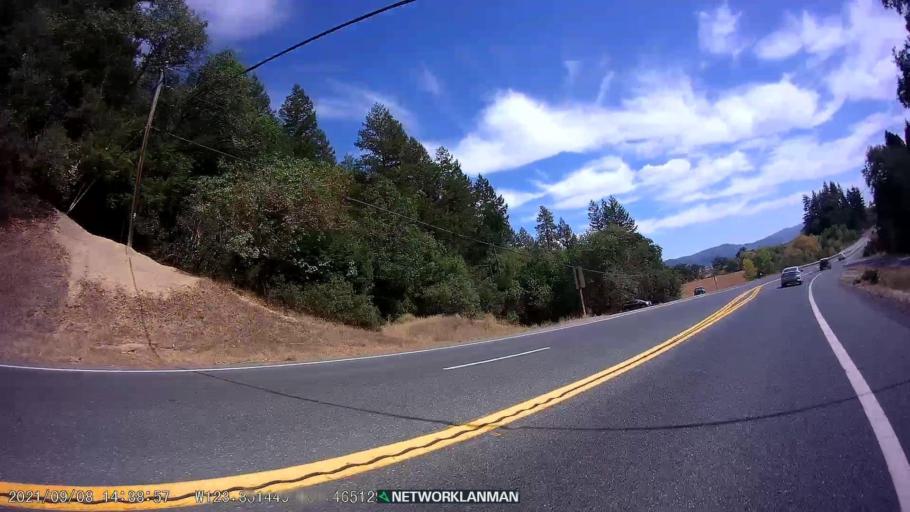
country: US
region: California
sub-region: Mendocino County
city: Brooktrails
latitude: 39.4651
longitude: -123.3508
